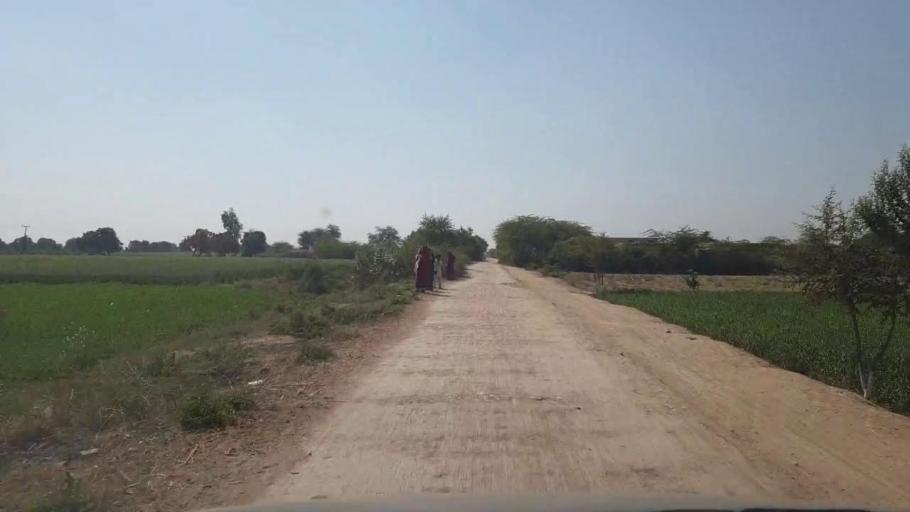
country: PK
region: Sindh
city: Digri
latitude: 25.2424
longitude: 69.2273
